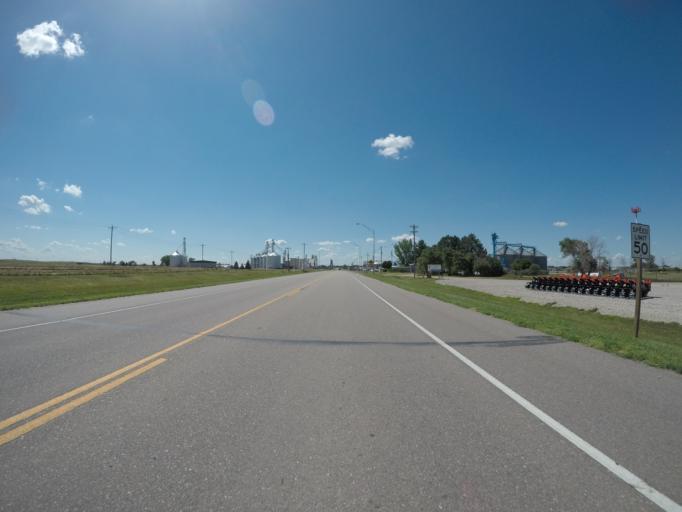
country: US
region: Nebraska
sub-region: Chase County
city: Imperial
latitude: 40.5083
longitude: -101.6315
